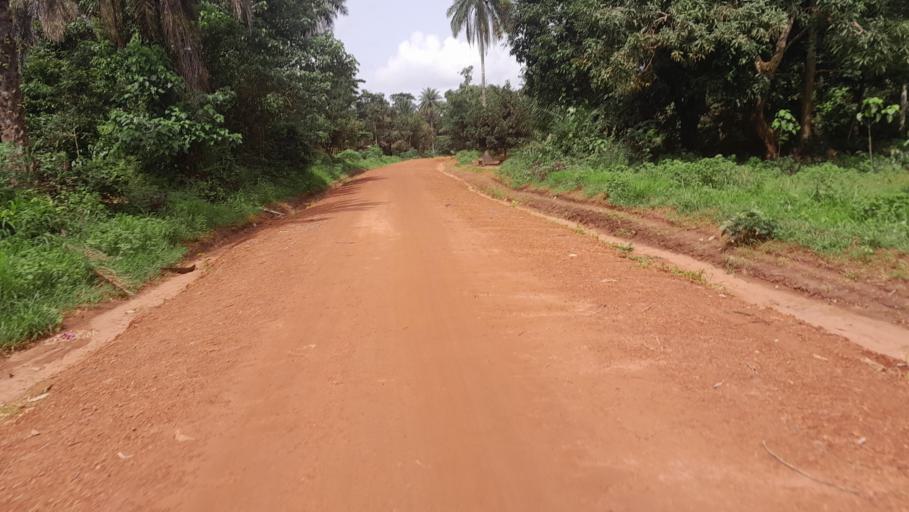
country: GN
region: Boke
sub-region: Boffa
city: Boffa
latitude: 10.0323
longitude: -13.8779
